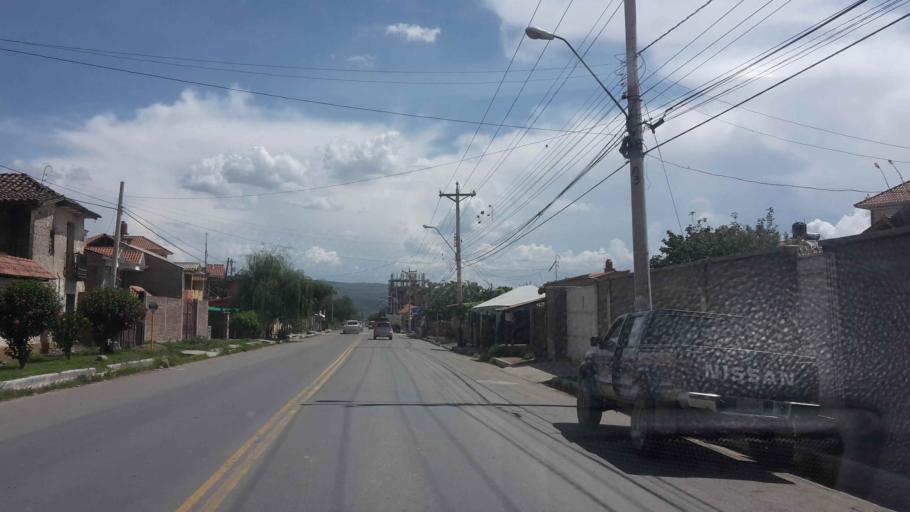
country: BO
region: Cochabamba
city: Cochabamba
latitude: -17.3752
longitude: -66.2336
